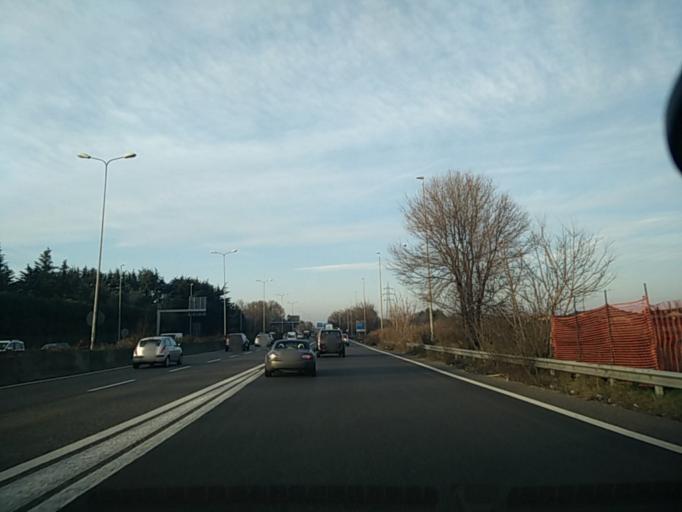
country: IT
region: Lombardy
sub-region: Citta metropolitana di Milano
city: Cusano Milanino
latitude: 45.5641
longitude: 9.1778
